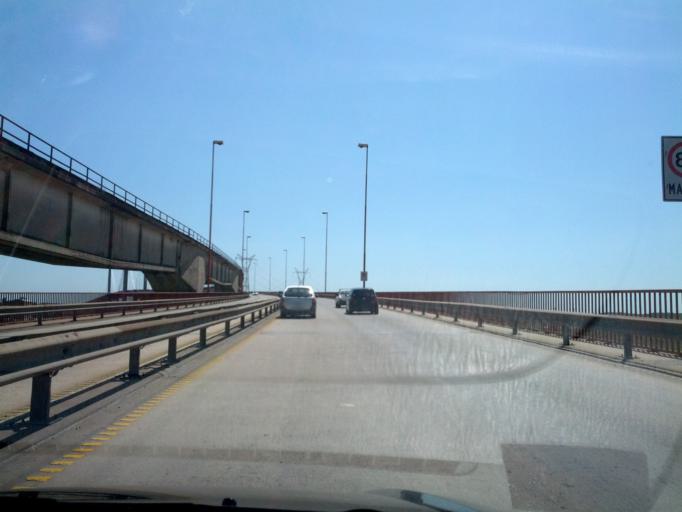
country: AR
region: Buenos Aires
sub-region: Partido de Zarate
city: Zarate
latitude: -34.1142
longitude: -59.0067
